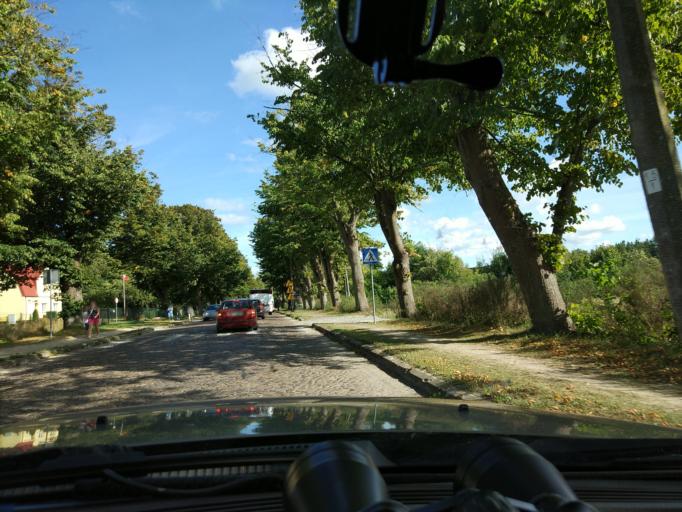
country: PL
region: Pomeranian Voivodeship
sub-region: Powiat pucki
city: Jastrzebia Gora
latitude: 54.8282
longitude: 18.3349
